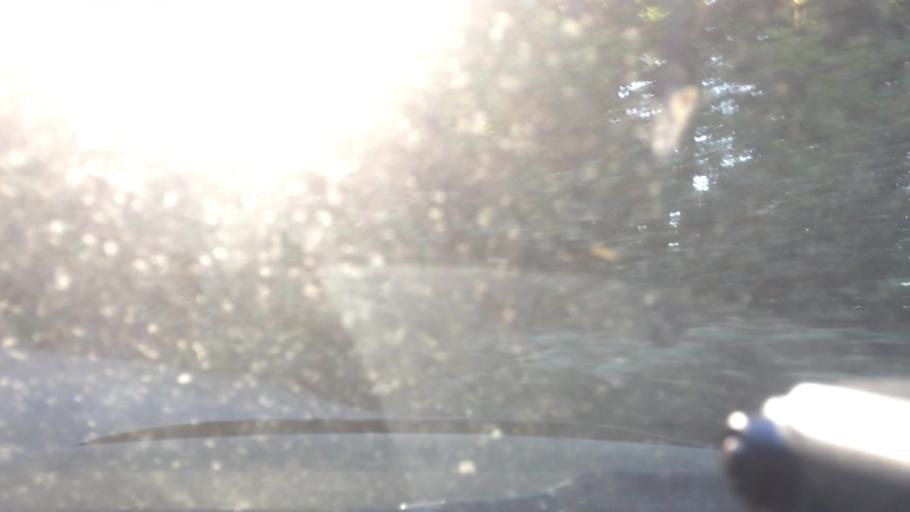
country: US
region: Oregon
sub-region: Yamhill County
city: Newberg
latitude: 45.3594
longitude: -122.9744
